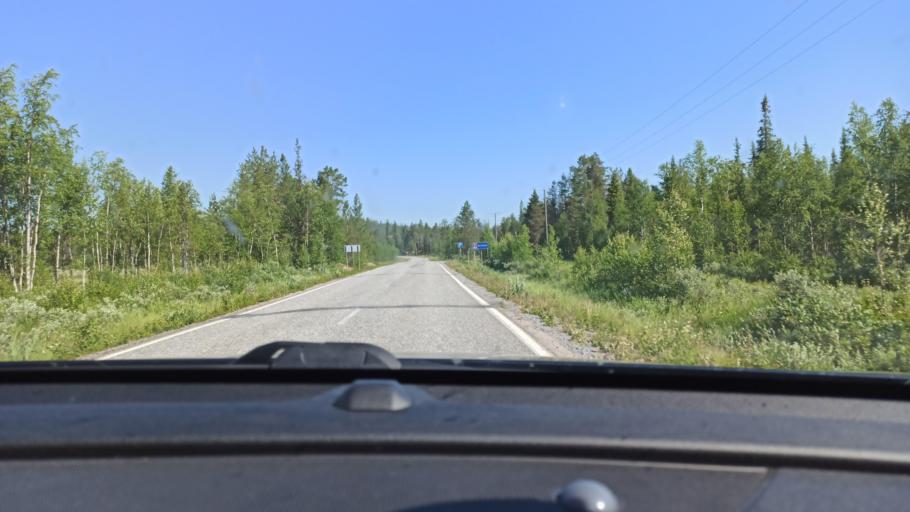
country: FI
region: Lapland
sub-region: Tunturi-Lappi
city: Kolari
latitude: 67.6310
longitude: 24.1575
